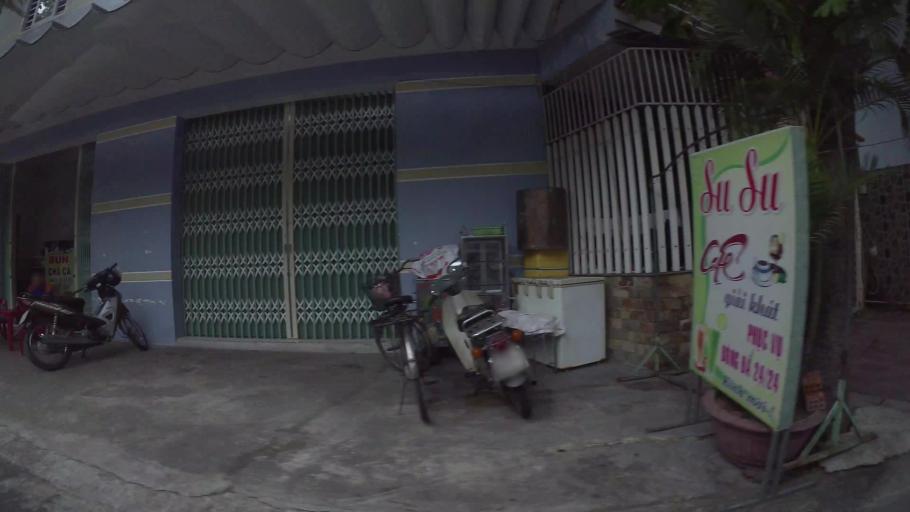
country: VN
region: Da Nang
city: Thanh Khe
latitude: 16.0620
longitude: 108.1899
